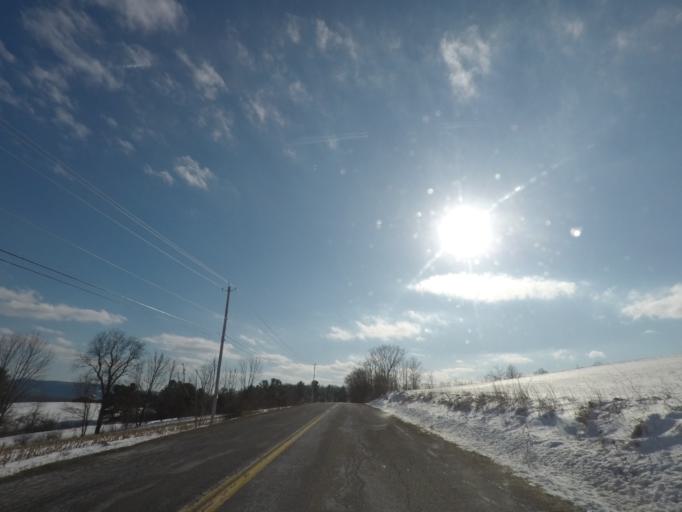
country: US
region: New York
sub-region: Rensselaer County
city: Hoosick Falls
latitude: 42.8631
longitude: -73.4951
